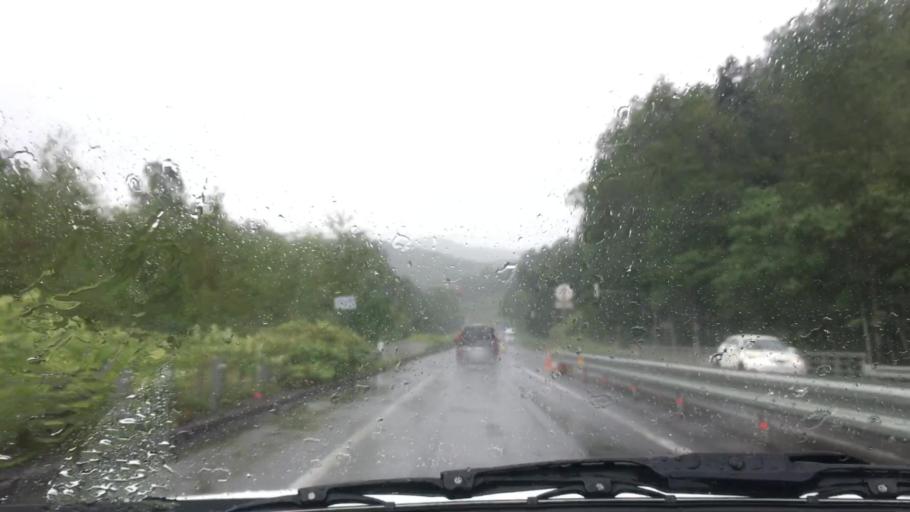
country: JP
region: Hokkaido
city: Otaru
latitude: 42.8481
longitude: 141.0495
